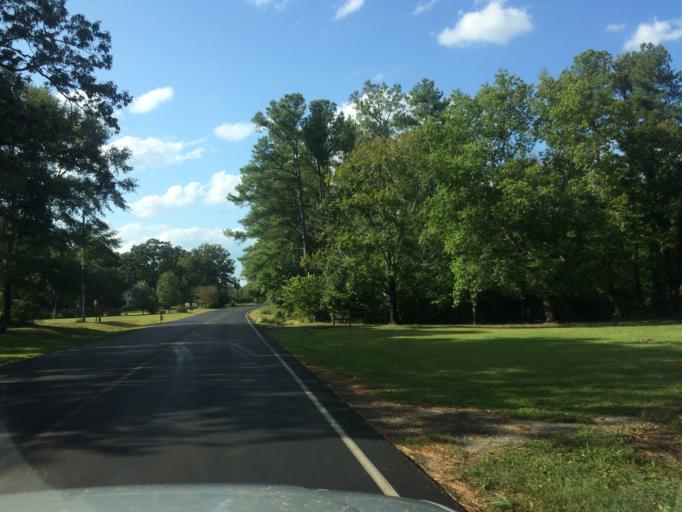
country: US
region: South Carolina
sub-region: Greenwood County
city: Ware Shoals
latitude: 34.5127
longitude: -82.1848
